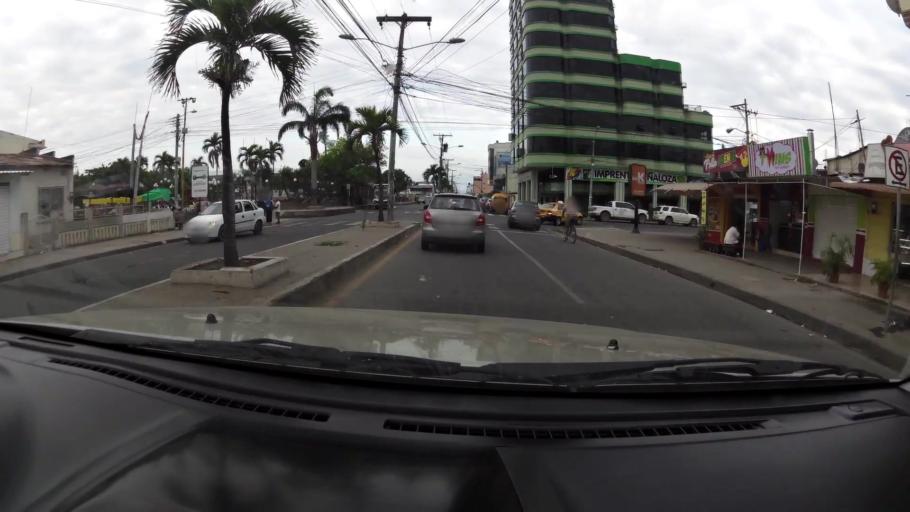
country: EC
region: El Oro
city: Machala
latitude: -3.2567
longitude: -79.9631
